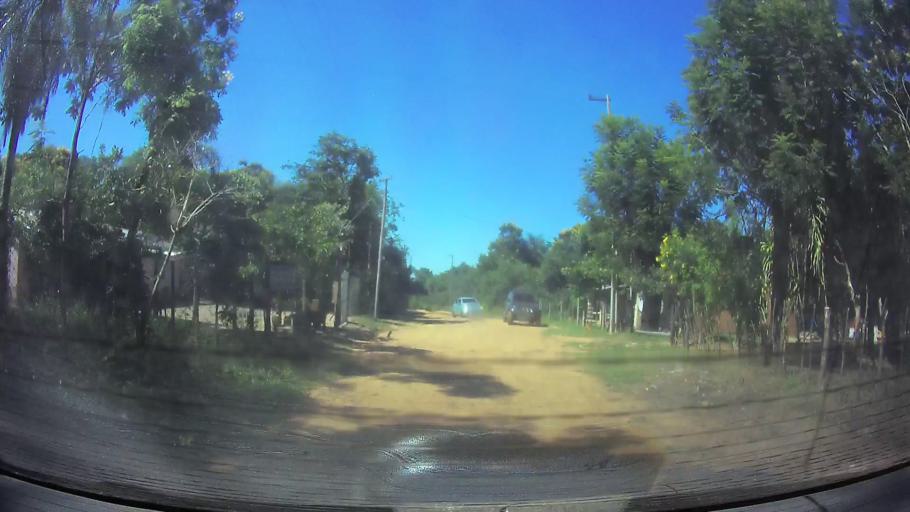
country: PY
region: Cordillera
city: Arroyos y Esteros
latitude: -24.9796
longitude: -57.2159
